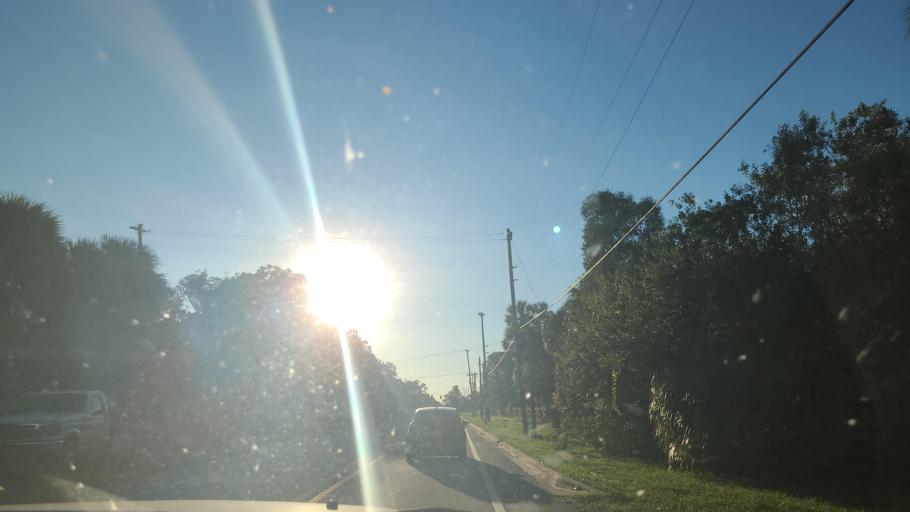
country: US
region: Florida
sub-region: Indian River County
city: Vero Beach South
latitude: 27.6094
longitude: -80.4284
